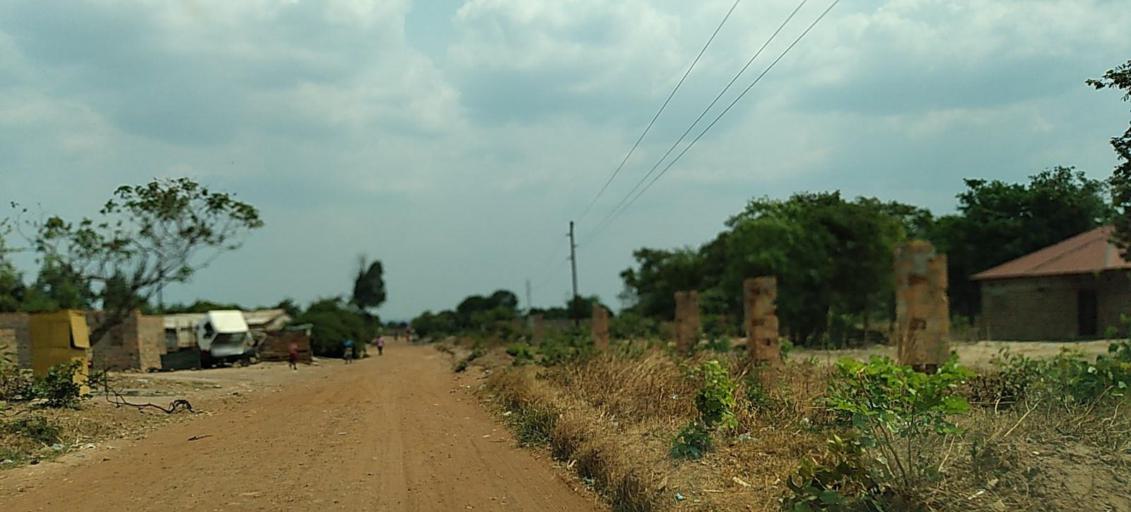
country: ZM
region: Copperbelt
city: Kalulushi
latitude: -12.8535
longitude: 28.0784
